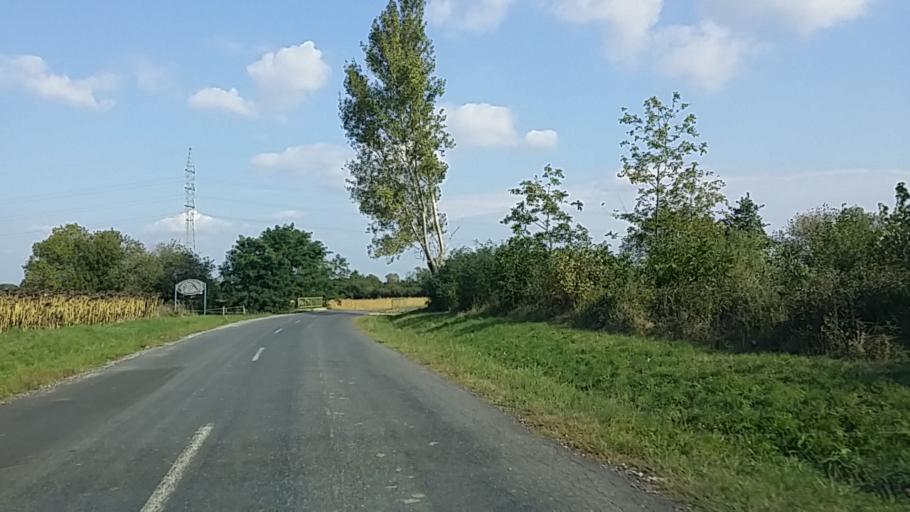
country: HU
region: Vas
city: Csepreg
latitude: 47.3835
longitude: 16.7148
